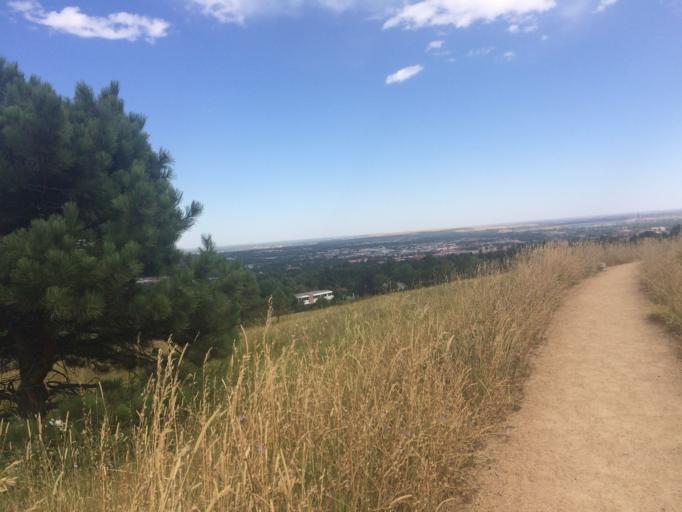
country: US
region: Colorado
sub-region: Boulder County
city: Boulder
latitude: 39.9983
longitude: -105.2891
